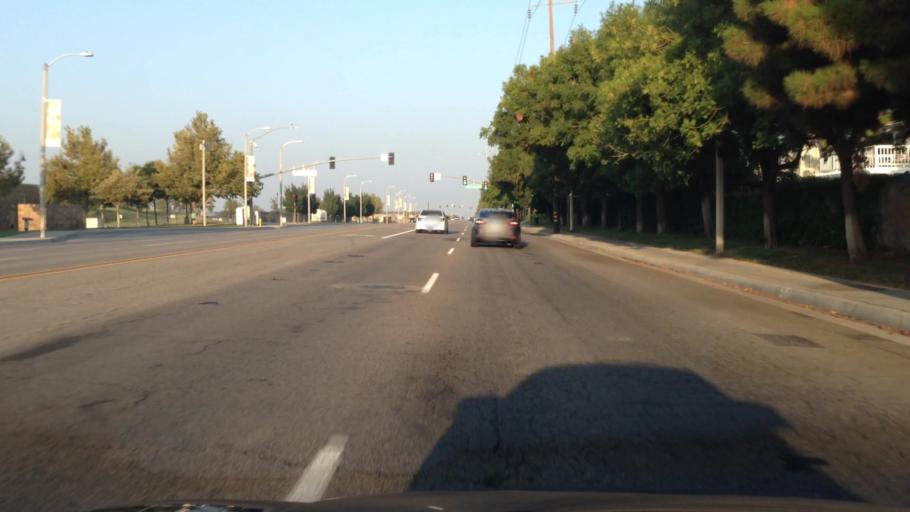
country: US
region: California
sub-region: Los Angeles County
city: Desert View Highlands
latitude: 34.6017
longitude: -118.1800
